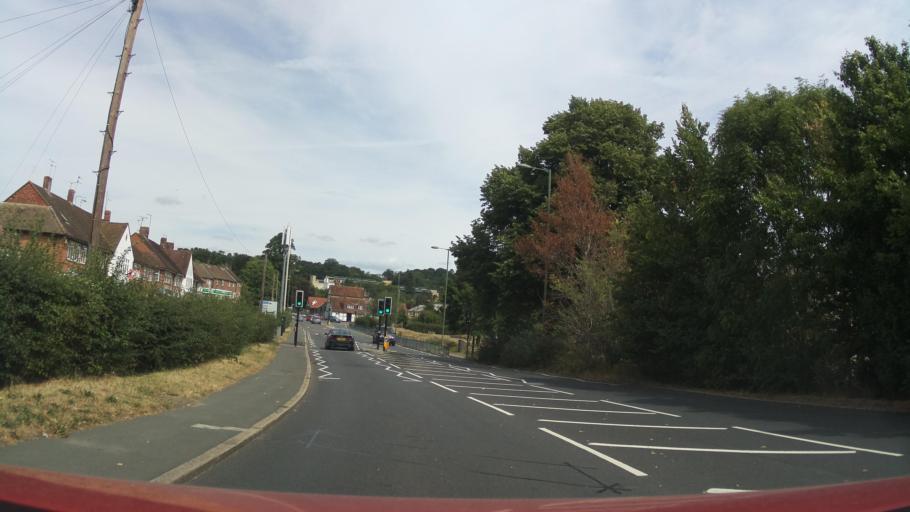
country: GB
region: England
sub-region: Surrey
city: Reigate
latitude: 51.2226
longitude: -0.1990
